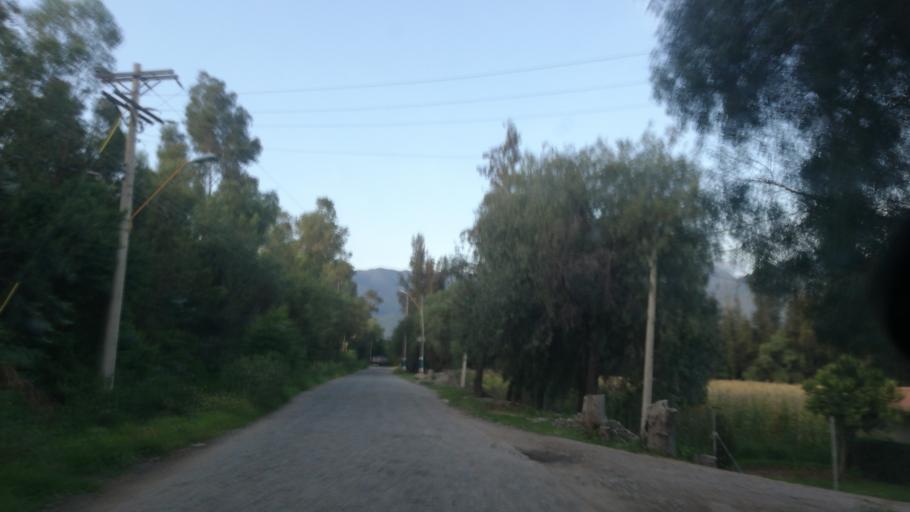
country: BO
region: Cochabamba
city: Cochabamba
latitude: -17.3724
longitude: -66.2074
